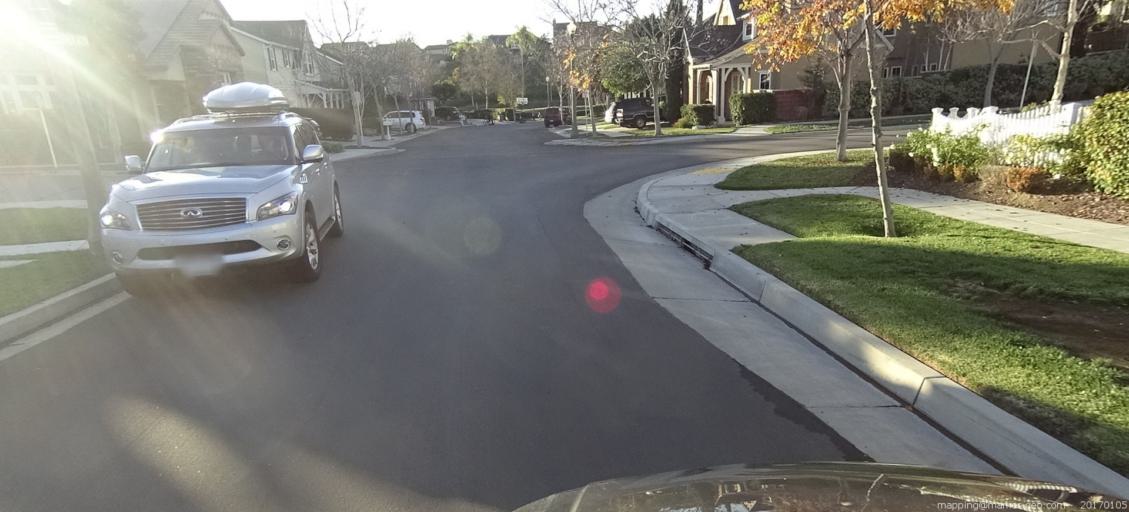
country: US
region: California
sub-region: Orange County
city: Ladera Ranch
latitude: 33.5569
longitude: -117.6345
